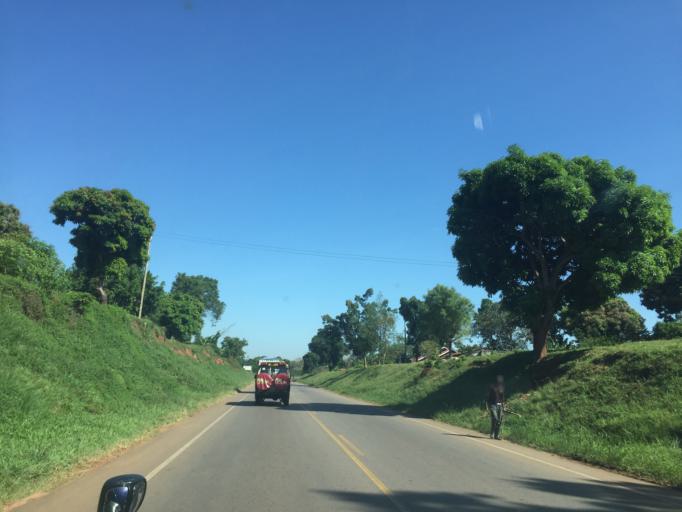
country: UG
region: Central Region
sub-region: Luwero District
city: Wobulenzi
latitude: 0.7559
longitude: 32.5145
